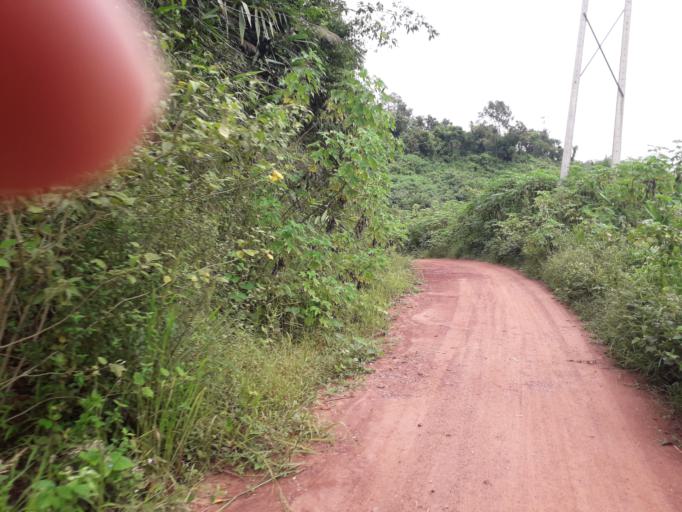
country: CN
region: Yunnan
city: Menglie
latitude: 22.2418
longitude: 101.6120
